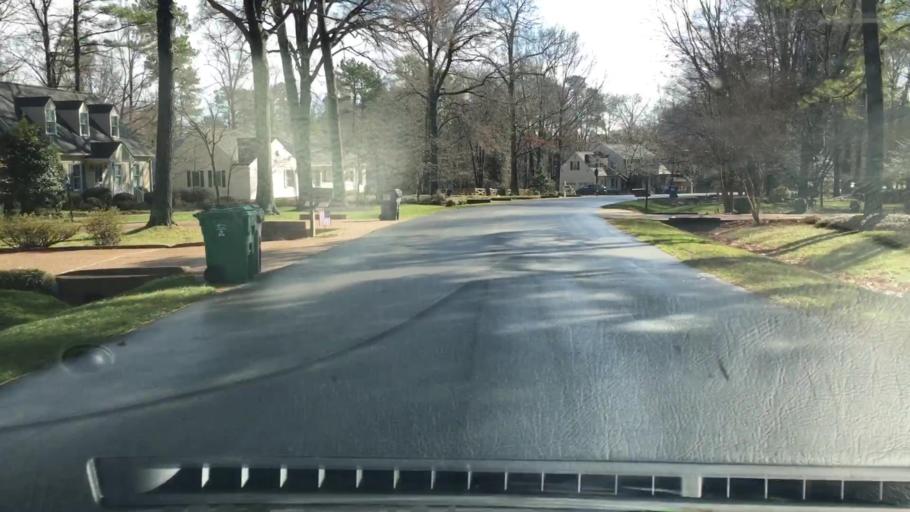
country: US
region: Virginia
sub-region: Chesterfield County
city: Bon Air
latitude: 37.5339
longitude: -77.6055
